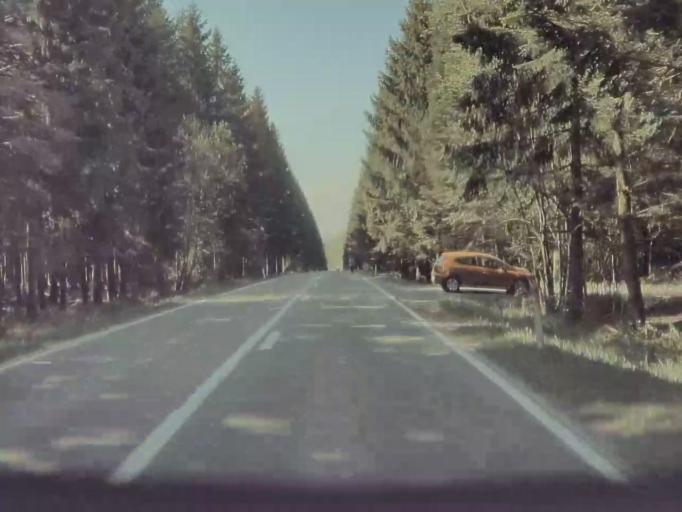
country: BE
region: Wallonia
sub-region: Province du Luxembourg
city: Libin
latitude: 50.0167
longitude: 5.2039
